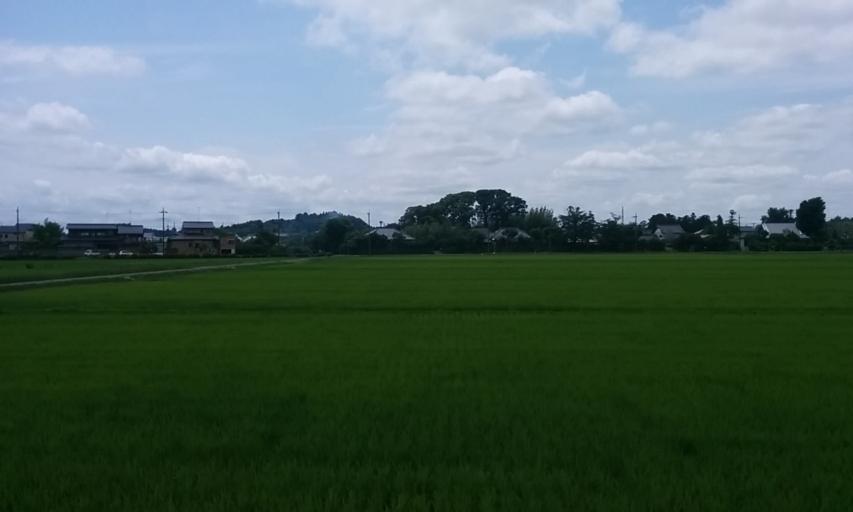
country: JP
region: Ibaraki
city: Edosaki
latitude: 35.8817
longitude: 140.3547
